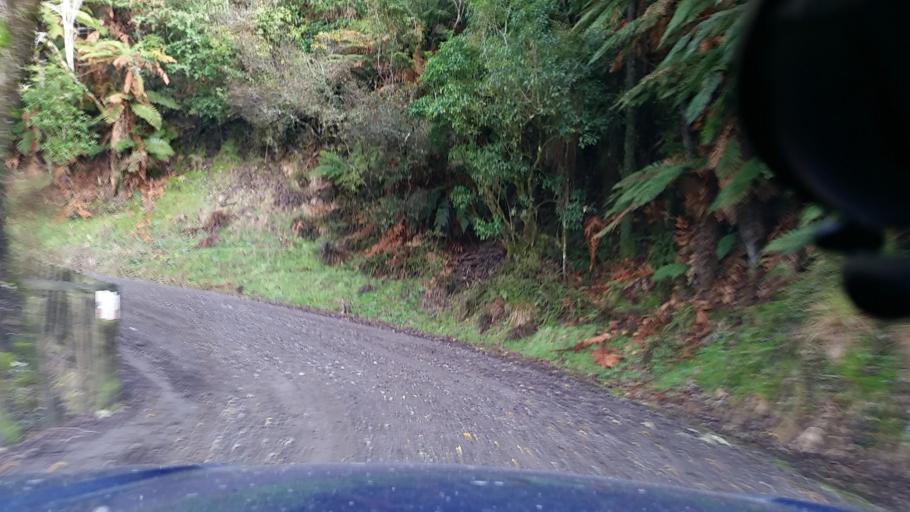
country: NZ
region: Taranaki
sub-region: New Plymouth District
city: Waitara
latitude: -39.0038
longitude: 174.7645
